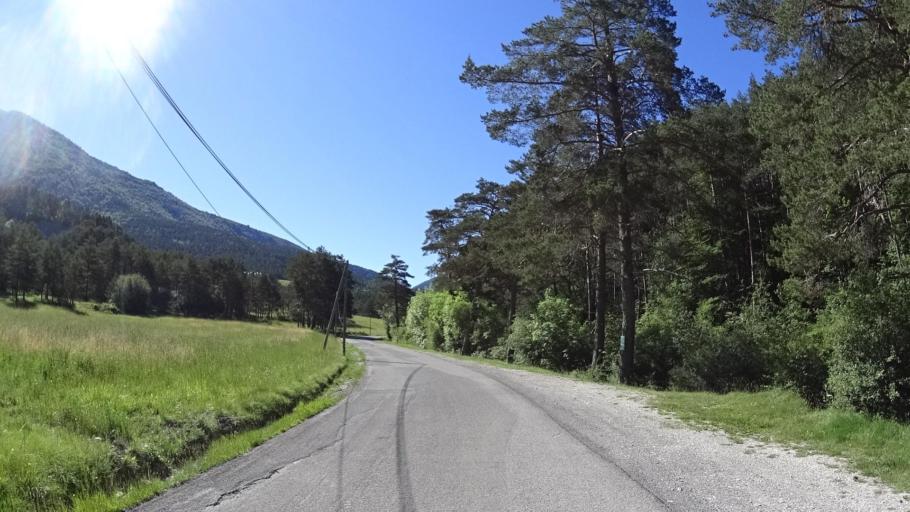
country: FR
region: Provence-Alpes-Cote d'Azur
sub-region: Departement des Alpes-de-Haute-Provence
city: Annot
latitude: 44.0000
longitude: 6.5721
